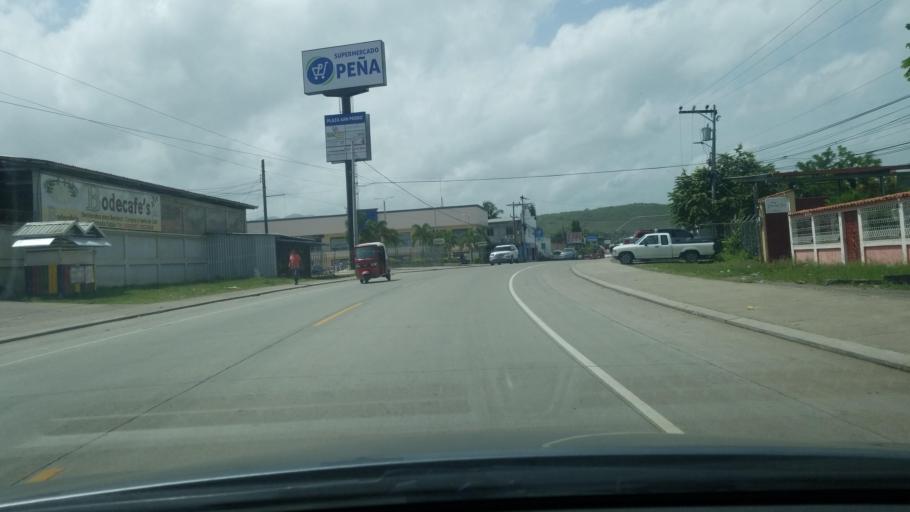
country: HN
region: Copan
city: La Entrada
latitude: 15.0650
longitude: -88.7583
